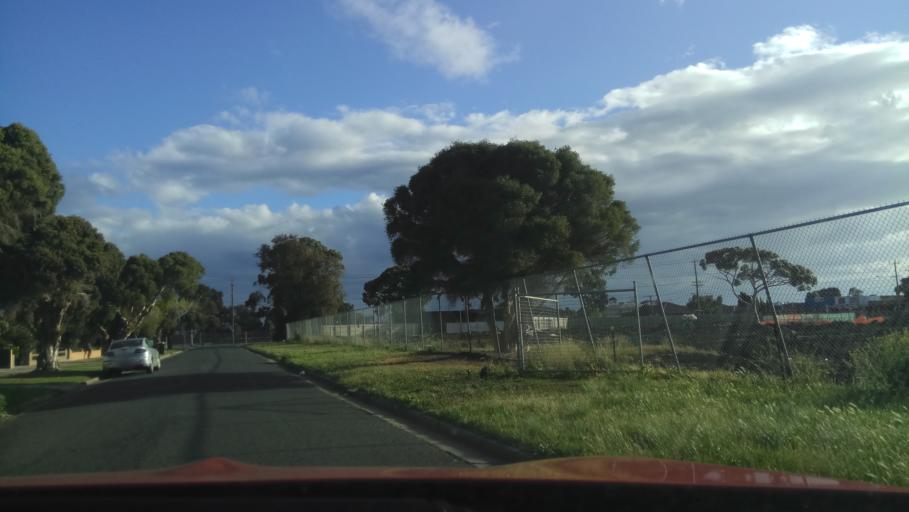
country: AU
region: Victoria
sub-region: Hobsons Bay
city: Altona North
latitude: -37.8293
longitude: 144.8412
